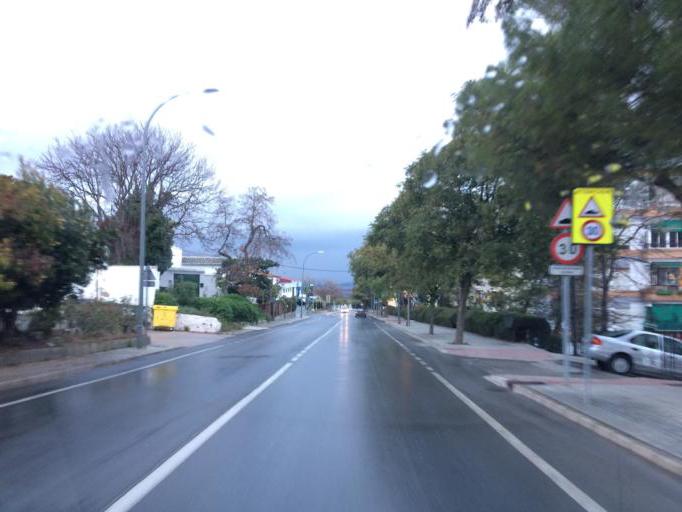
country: ES
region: Andalusia
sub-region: Provincia de Malaga
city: Antequera
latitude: 37.0241
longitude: -4.5610
